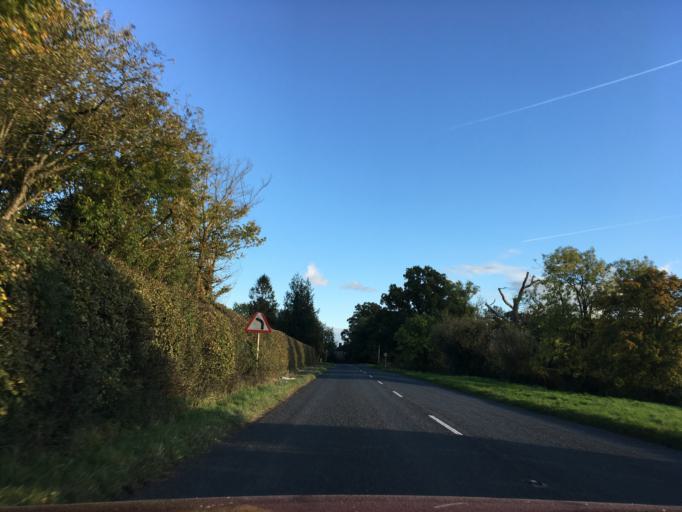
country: GB
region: England
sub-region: Worcestershire
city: Upton upon Severn
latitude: 52.0004
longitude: -2.2337
